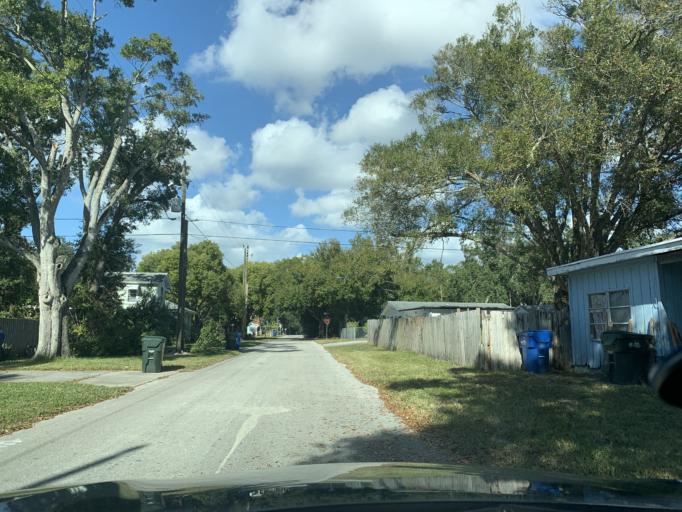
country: US
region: Florida
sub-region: Pinellas County
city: Belleair
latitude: 27.9293
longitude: -82.7981
